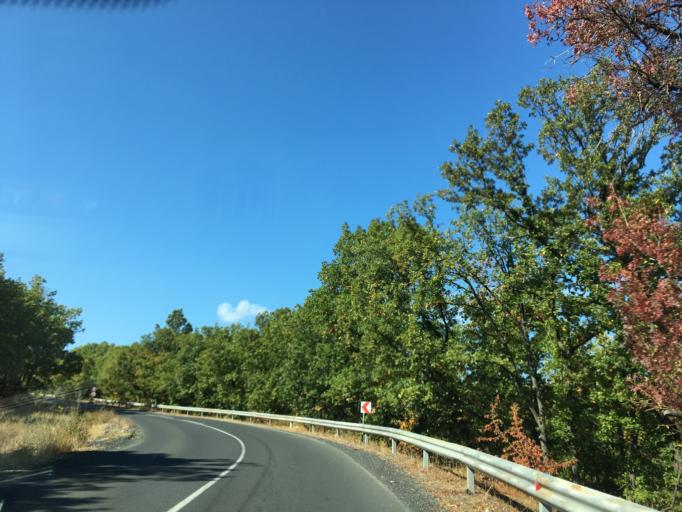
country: BG
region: Kurdzhali
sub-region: Obshtina Krumovgrad
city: Krumovgrad
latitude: 41.4736
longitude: 25.5443
